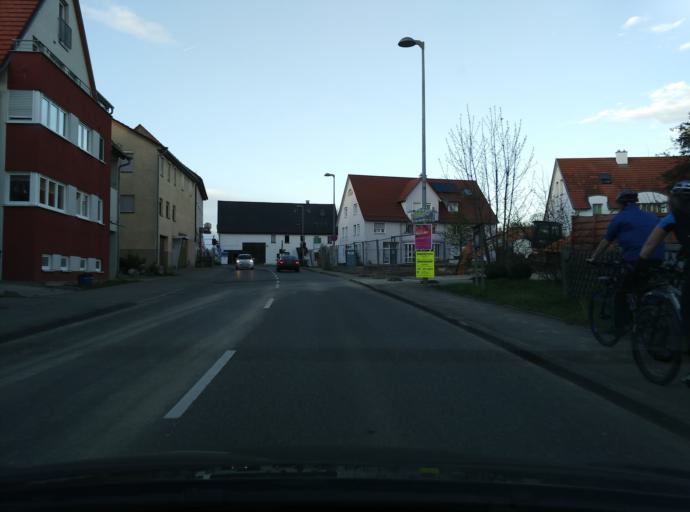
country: DE
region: Baden-Wuerttemberg
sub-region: Regierungsbezirk Stuttgart
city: Grossbettlingen
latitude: 48.5665
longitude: 9.3062
